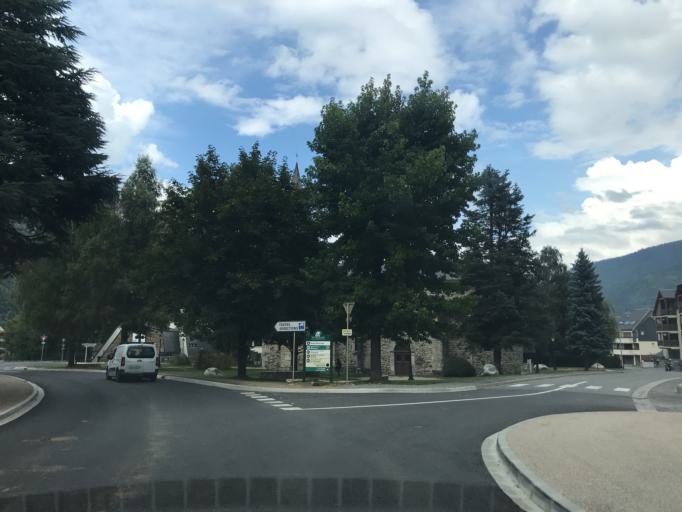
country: FR
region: Midi-Pyrenees
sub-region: Departement des Hautes-Pyrenees
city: Saint-Lary-Soulan
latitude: 42.8192
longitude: 0.3228
